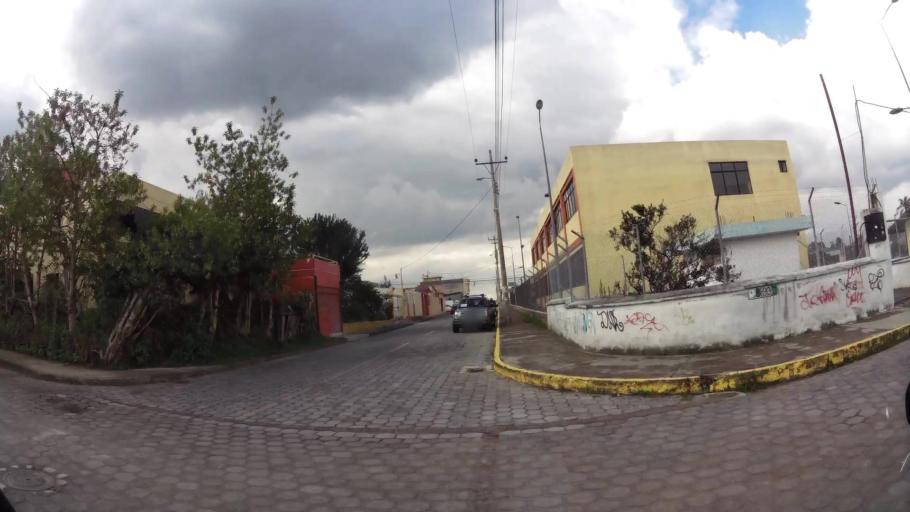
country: EC
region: Pichincha
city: Sangolqui
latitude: -0.3256
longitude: -78.4629
